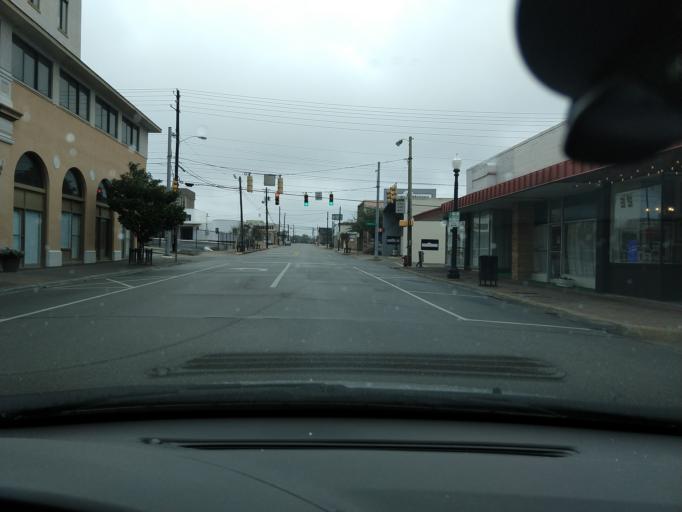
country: US
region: Alabama
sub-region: Houston County
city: Dothan
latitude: 31.2262
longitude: -85.3924
